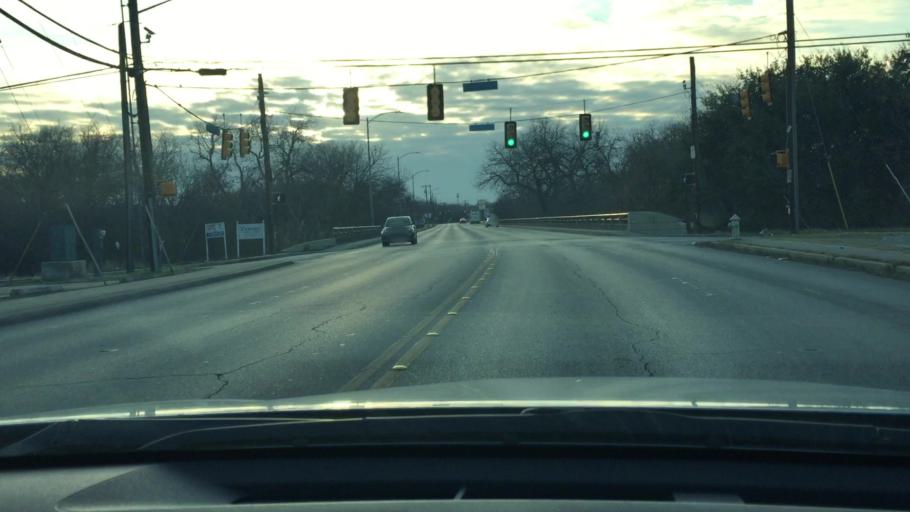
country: US
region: Texas
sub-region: Bexar County
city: Terrell Hills
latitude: 29.4966
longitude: -98.4204
